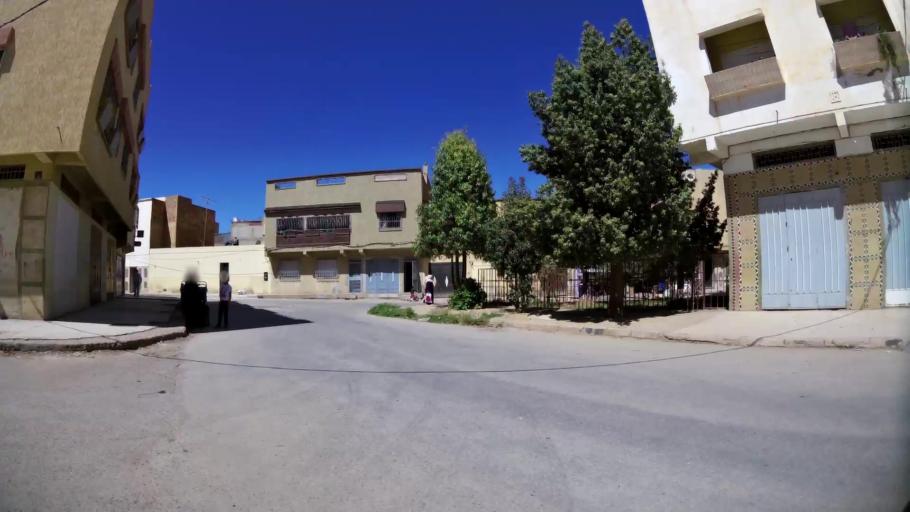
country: MA
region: Oriental
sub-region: Oujda-Angad
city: Oujda
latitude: 34.6681
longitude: -1.9347
